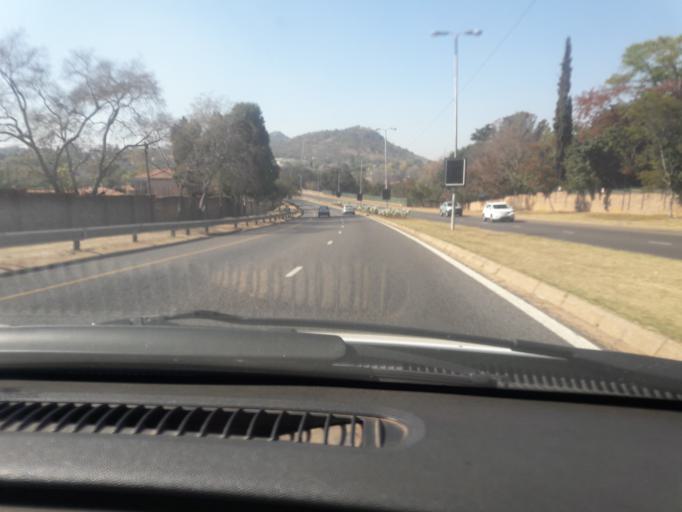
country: ZA
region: Gauteng
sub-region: City of Tshwane Metropolitan Municipality
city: Pretoria
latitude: -25.7680
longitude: 28.2841
